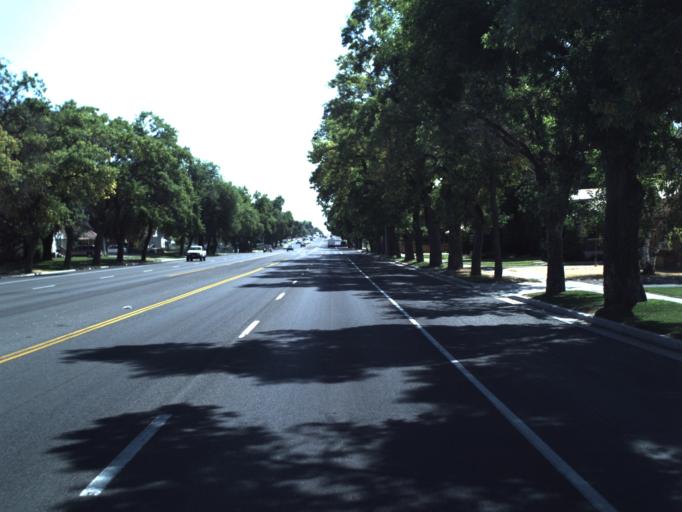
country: US
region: Utah
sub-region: Cache County
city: Smithfield
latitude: 41.8446
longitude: -111.8326
